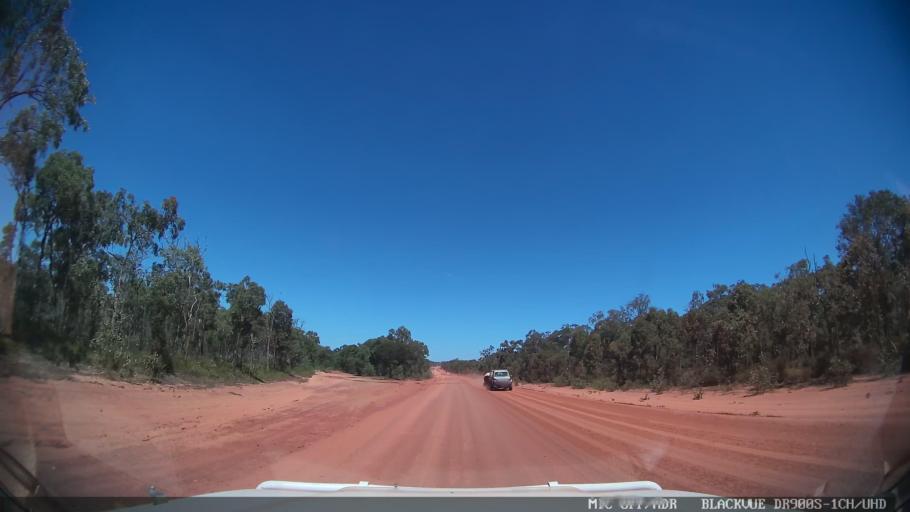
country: AU
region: Queensland
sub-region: Torres
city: Thursday Island
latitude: -11.3653
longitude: 142.3464
